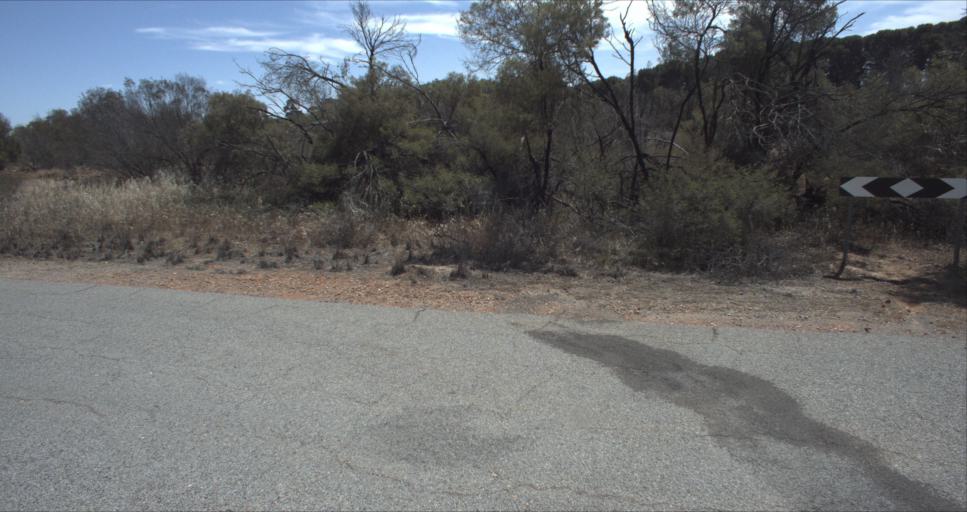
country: AU
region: New South Wales
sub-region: Leeton
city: Leeton
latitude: -34.6706
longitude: 146.4437
